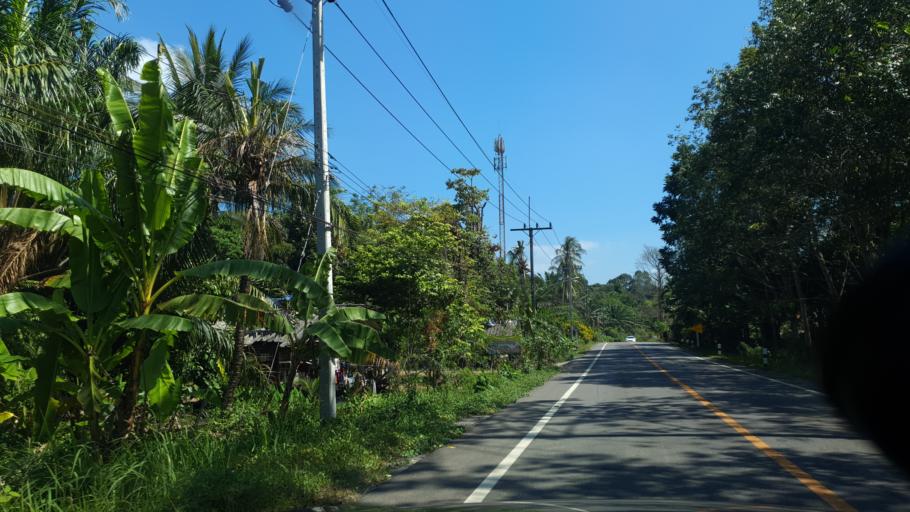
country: TH
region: Krabi
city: Khlong Thom
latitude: 7.9216
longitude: 99.2474
